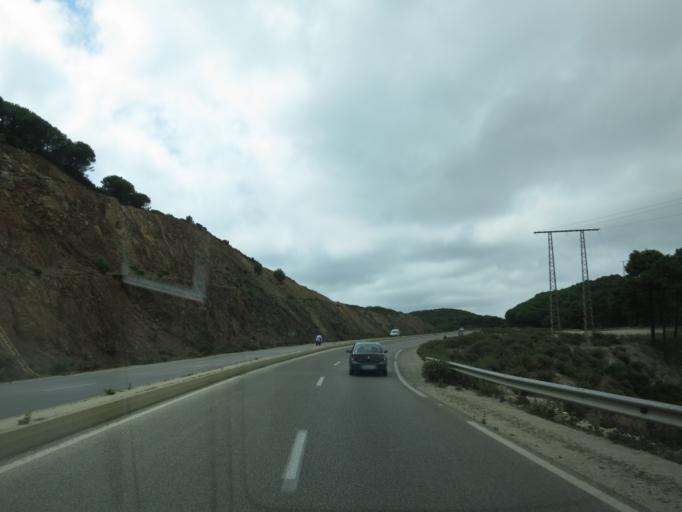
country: ES
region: Ceuta
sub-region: Ceuta
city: Ceuta
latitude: 35.8638
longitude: -5.4113
